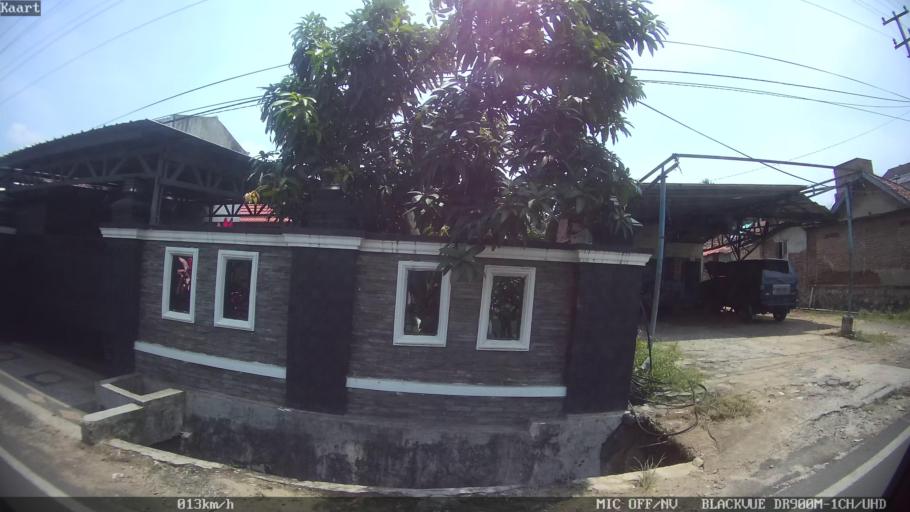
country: ID
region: Lampung
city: Bandarlampung
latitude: -5.4447
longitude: 105.2560
